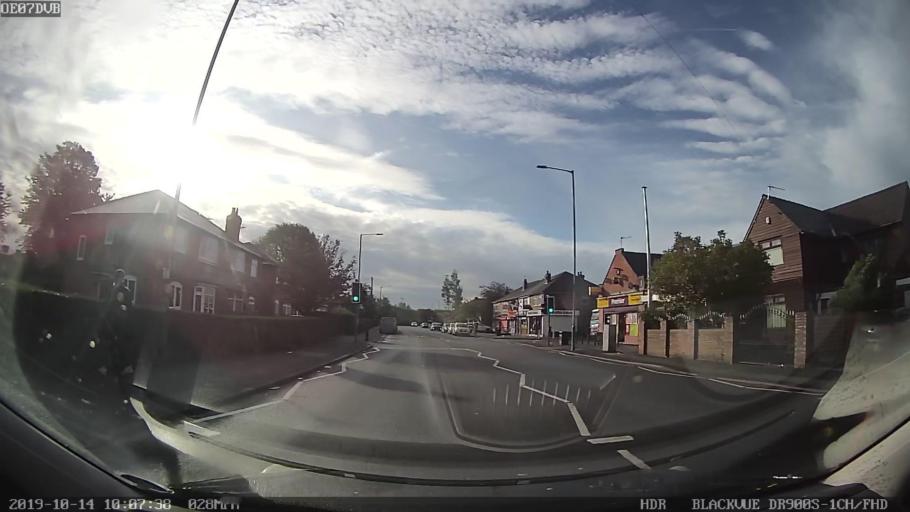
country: GB
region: England
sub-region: Manchester
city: Failsworth
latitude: 53.5213
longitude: -2.1821
